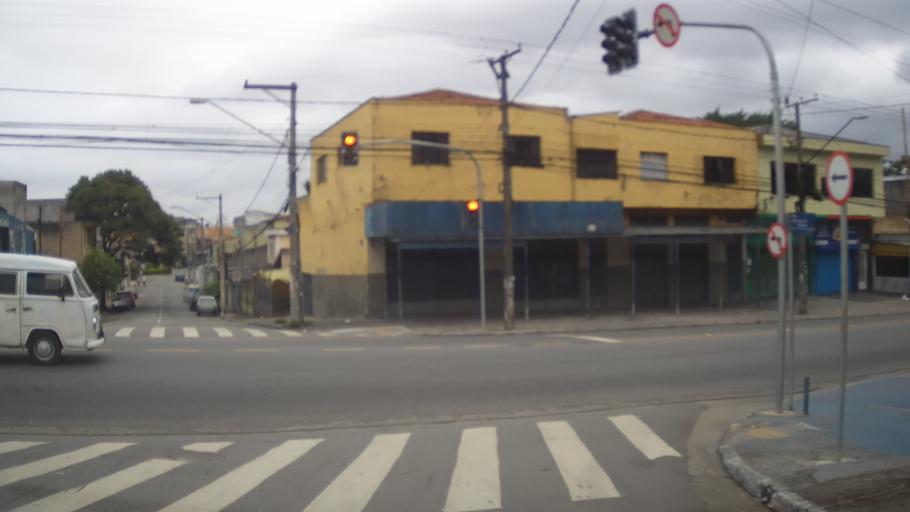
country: BR
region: Sao Paulo
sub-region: Guarulhos
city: Guarulhos
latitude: -23.4494
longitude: -46.5086
